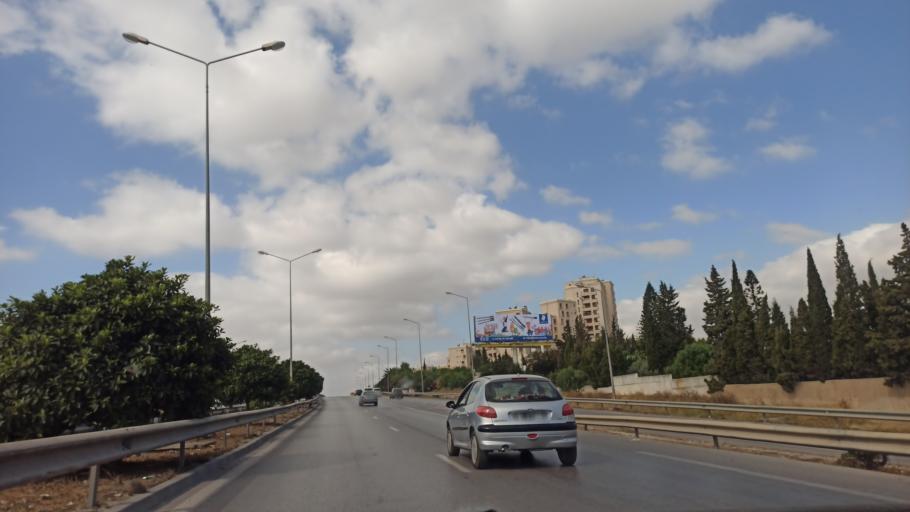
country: TN
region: Ariana
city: Ariana
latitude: 36.8468
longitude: 10.1811
